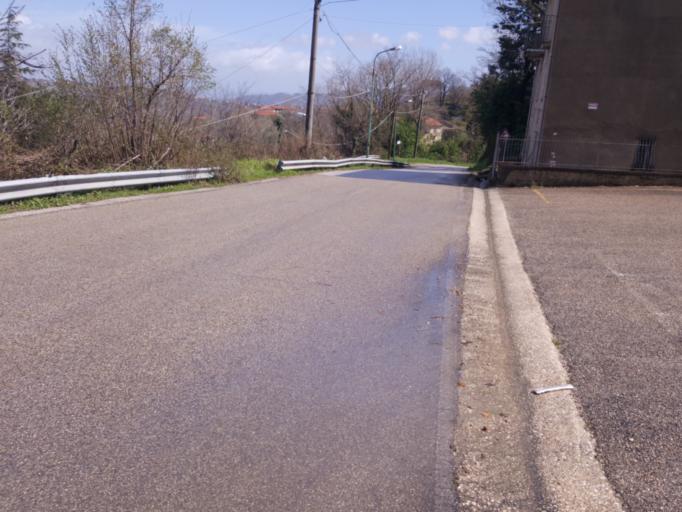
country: IT
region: Campania
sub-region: Provincia di Avellino
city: Roccabascerana
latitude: 41.0400
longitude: 14.7134
